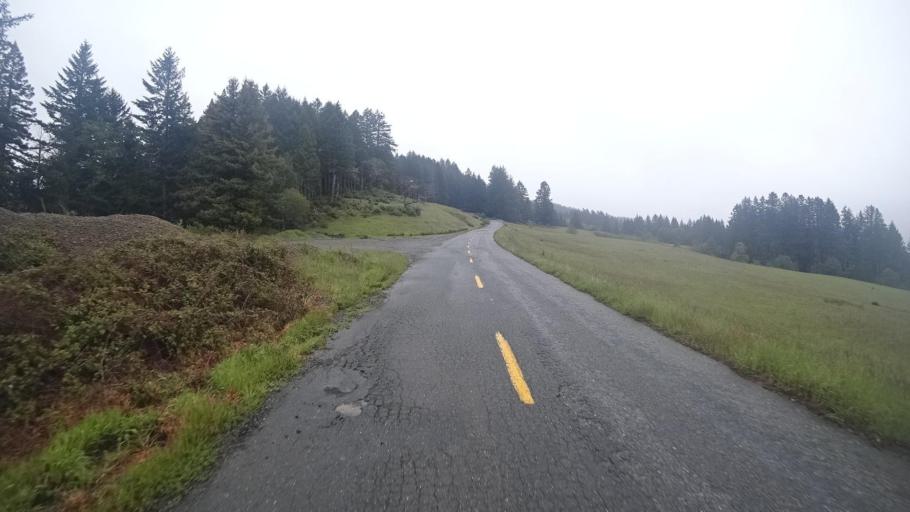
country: US
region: California
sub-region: Humboldt County
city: Westhaven-Moonstone
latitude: 41.2279
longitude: -123.9682
